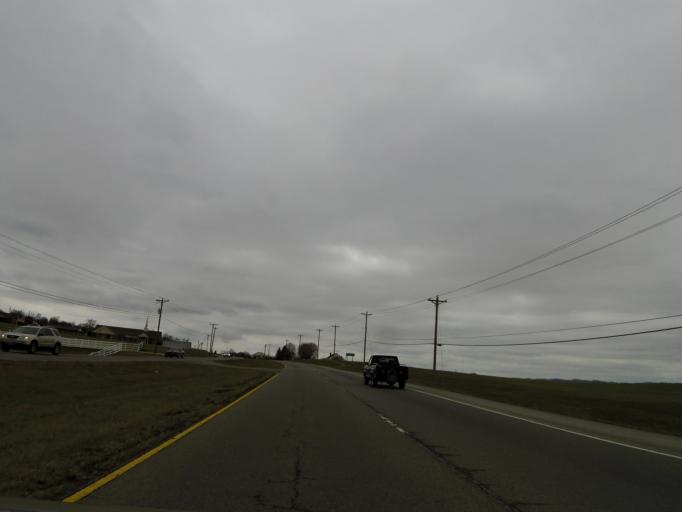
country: US
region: Tennessee
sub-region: Jefferson County
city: Jefferson City
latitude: 36.1557
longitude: -83.4242
